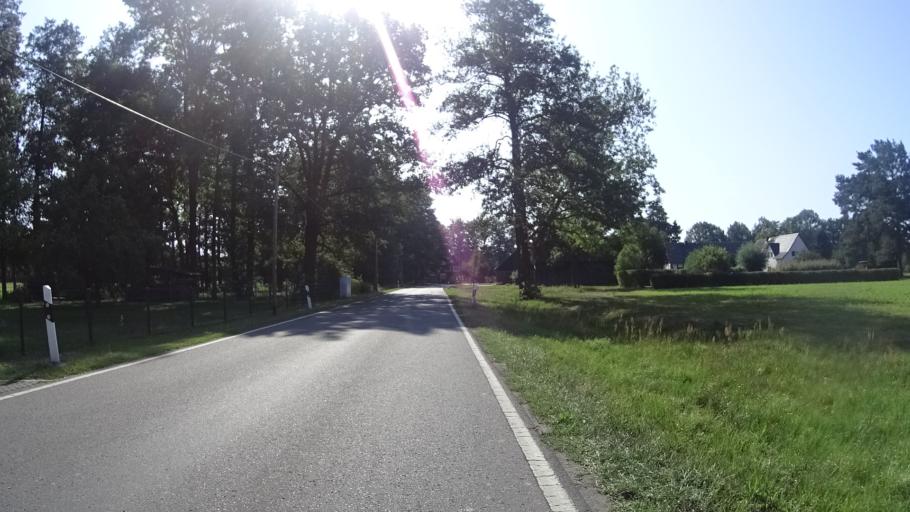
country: DE
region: Brandenburg
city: Burg
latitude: 51.8657
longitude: 14.1253
